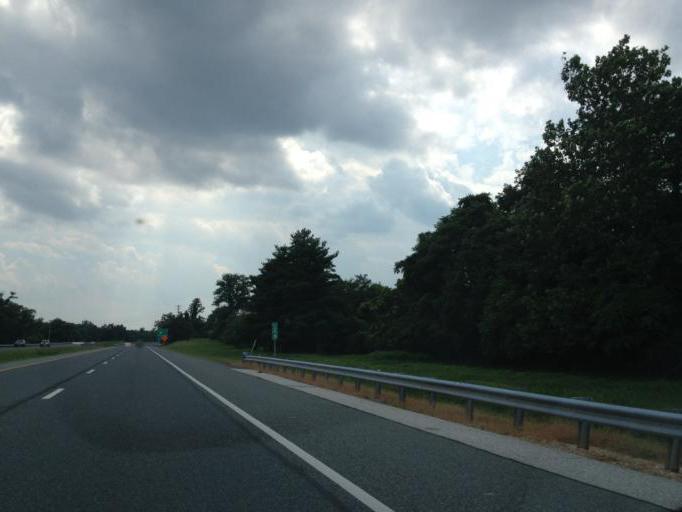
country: US
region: Maryland
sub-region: Baltimore County
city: Lansdowne
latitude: 39.2257
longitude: -76.6803
